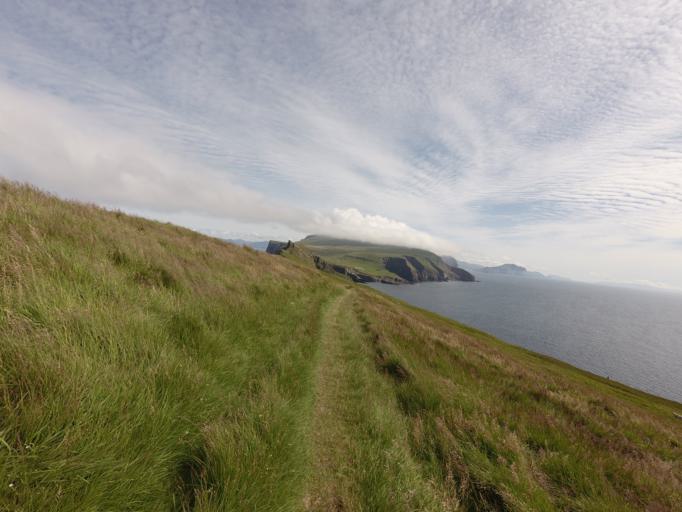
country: FO
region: Vagar
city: Sorvagur
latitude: 62.0996
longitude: -7.6749
